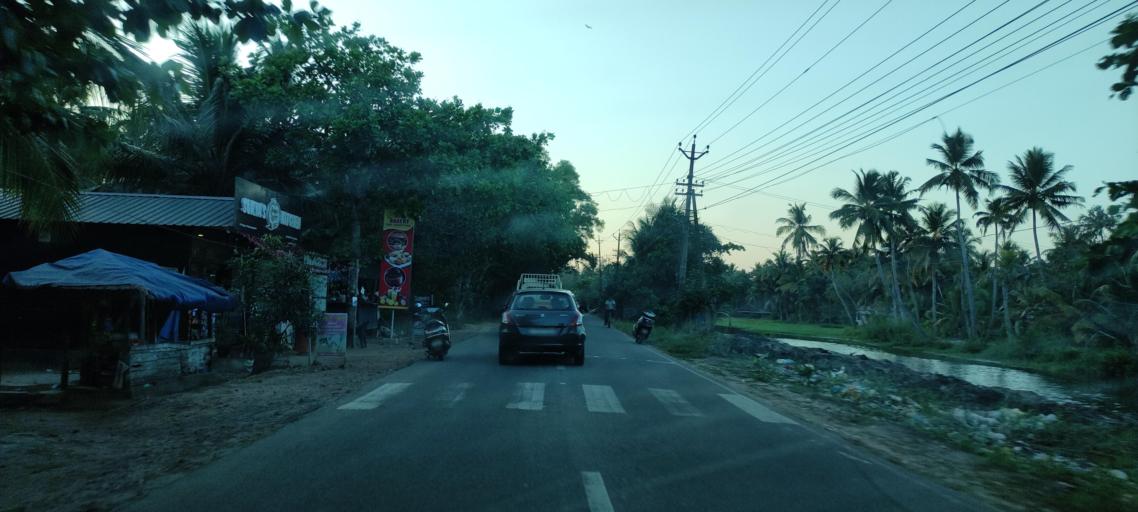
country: IN
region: Kerala
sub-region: Alappuzha
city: Kayankulam
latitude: 9.2577
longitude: 76.4169
